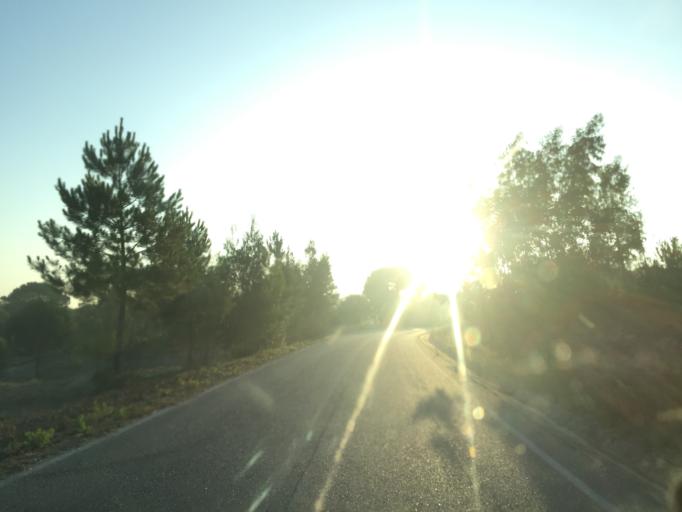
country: PT
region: Santarem
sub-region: Coruche
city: Coruche
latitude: 39.0483
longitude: -8.4319
